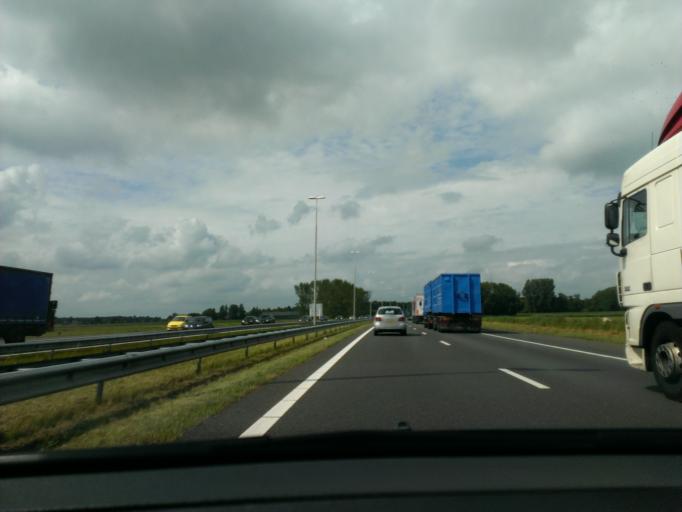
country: NL
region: Gelderland
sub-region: Gemeente Epe
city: Vaassen
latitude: 52.2602
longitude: 6.0021
